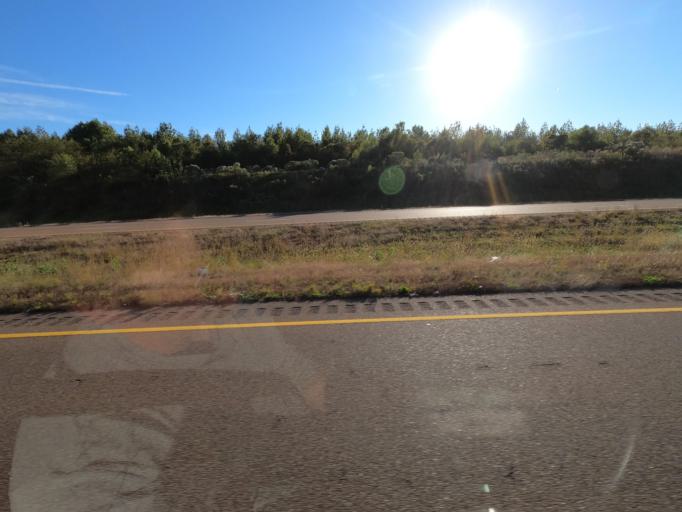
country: US
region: Tennessee
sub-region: Fayette County
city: Piperton
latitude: 35.0703
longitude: -89.6432
